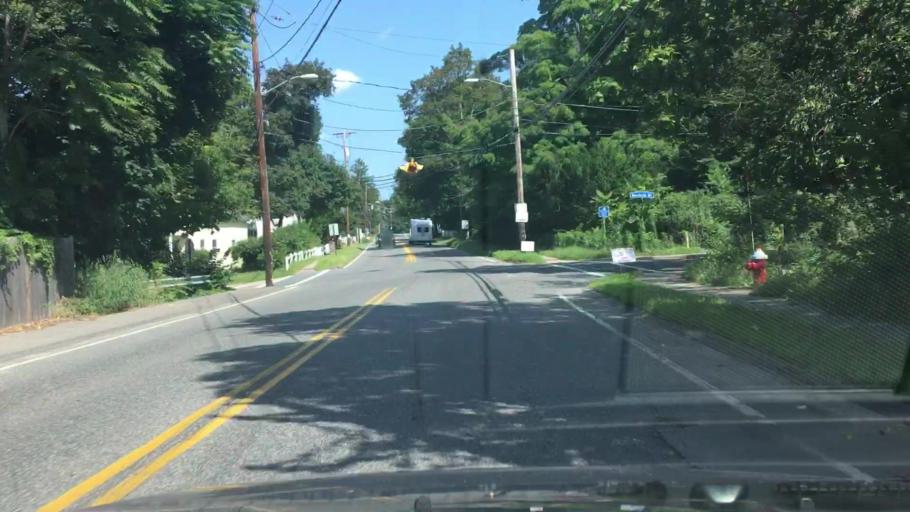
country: US
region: Massachusetts
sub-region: Middlesex County
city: Holliston
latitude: 42.2003
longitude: -71.4241
